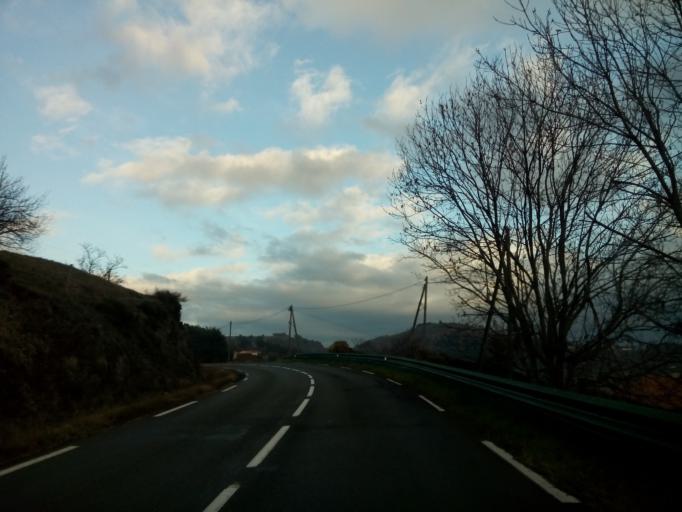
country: FR
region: Rhone-Alpes
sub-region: Departement de la Loire
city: Bourg-Argental
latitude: 45.3025
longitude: 4.5754
